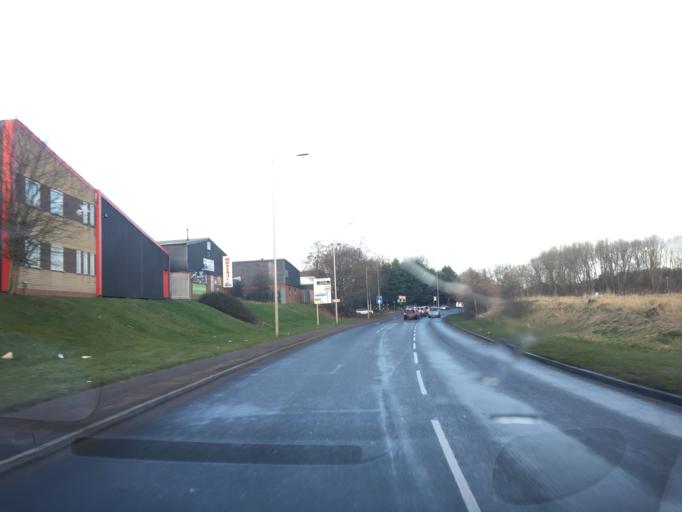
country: GB
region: England
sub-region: Warwickshire
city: Rugby
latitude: 52.3819
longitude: -1.2458
